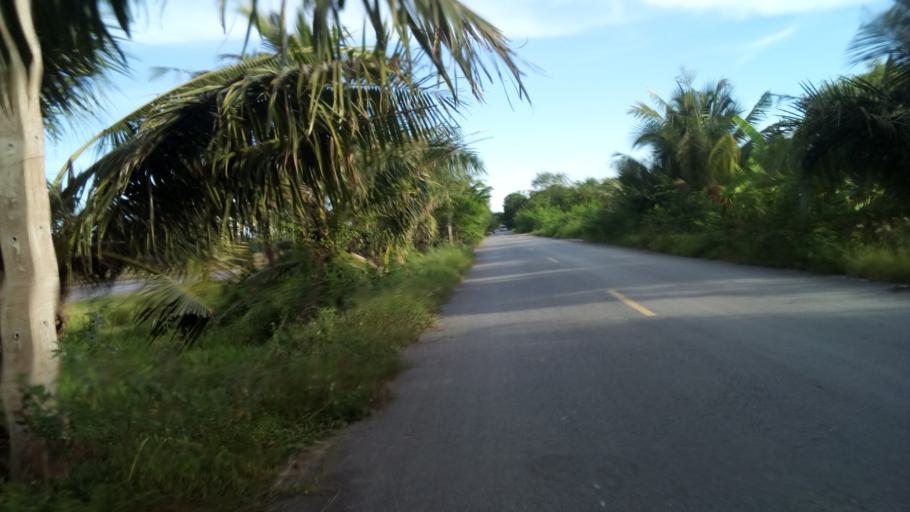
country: TH
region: Pathum Thani
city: Ban Lam Luk Ka
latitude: 14.0145
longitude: 100.8461
